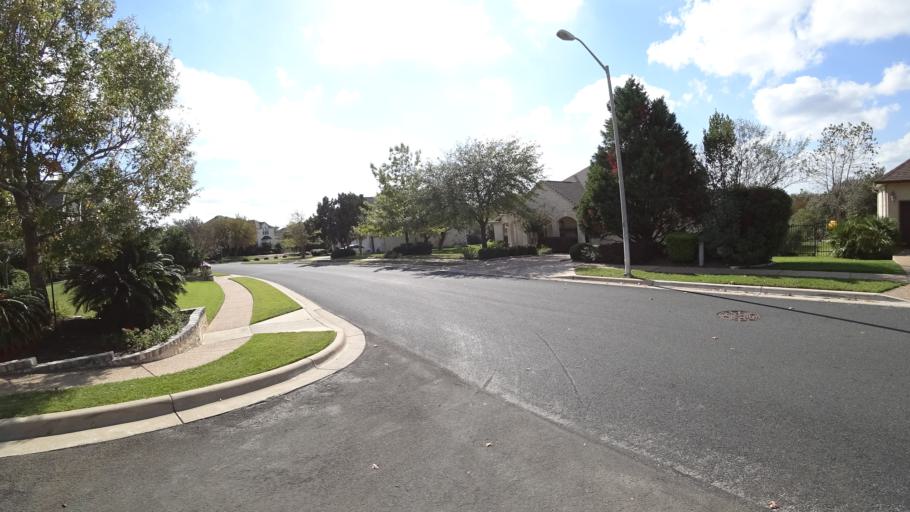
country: US
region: Texas
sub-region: Williamson County
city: Anderson Mill
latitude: 30.4254
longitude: -97.8062
